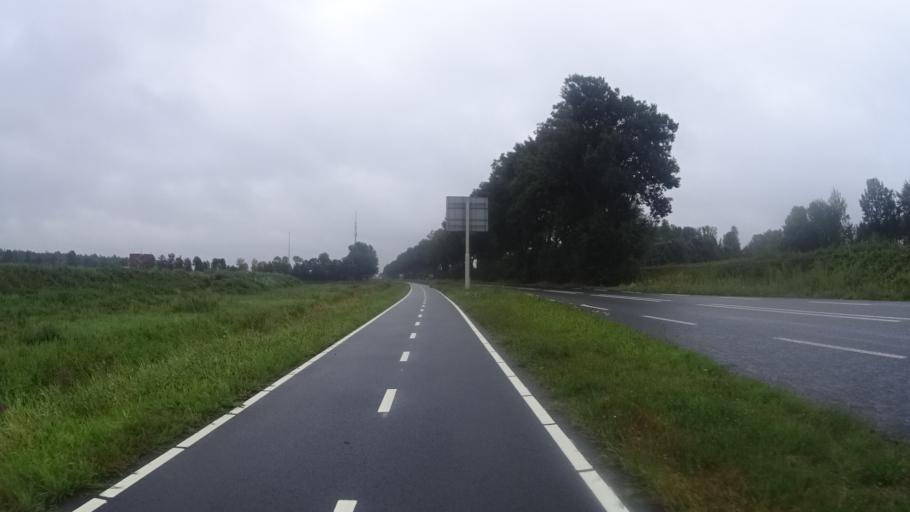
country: NL
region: Groningen
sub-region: Gemeente  Oldambt
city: Winschoten
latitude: 53.1640
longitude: 7.0024
